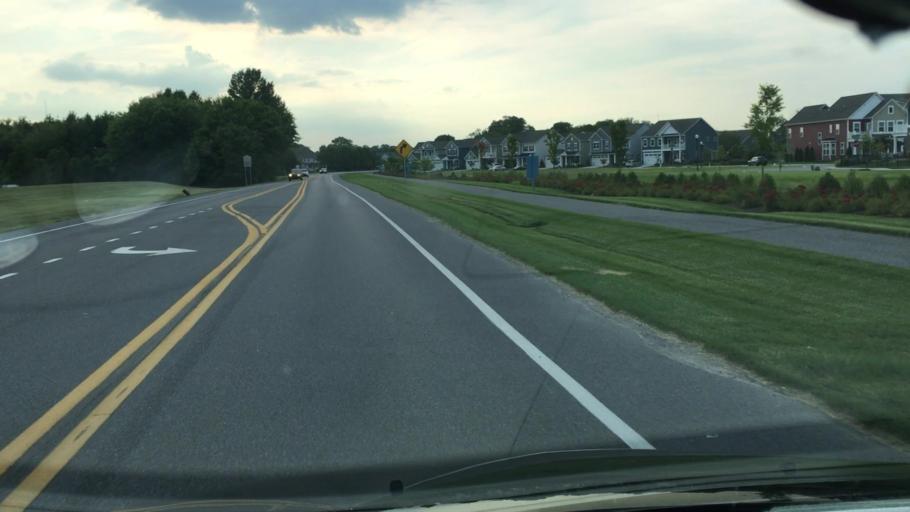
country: US
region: Delaware
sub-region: Sussex County
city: Ocean View
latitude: 38.5257
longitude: -75.0774
